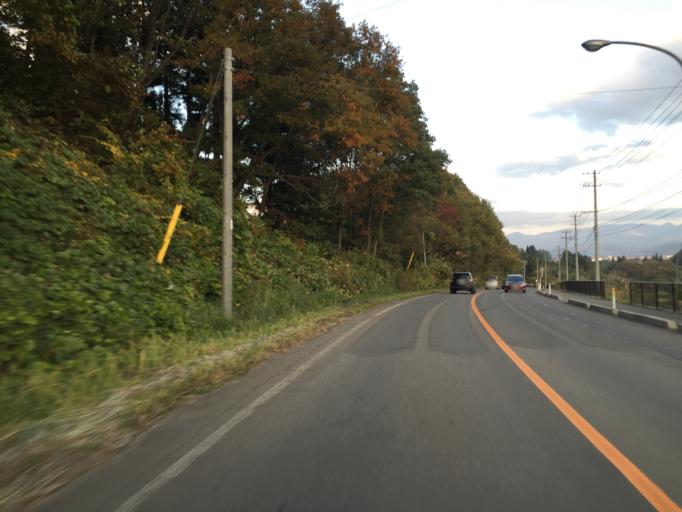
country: JP
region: Yamagata
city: Yonezawa
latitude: 37.9152
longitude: 140.0559
